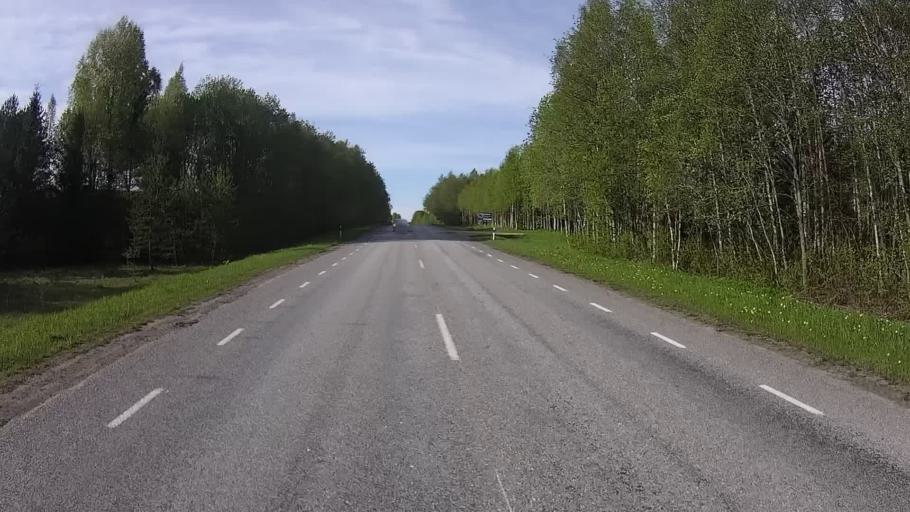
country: EE
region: Tartu
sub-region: Elva linn
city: Elva
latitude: 58.1454
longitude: 26.5238
